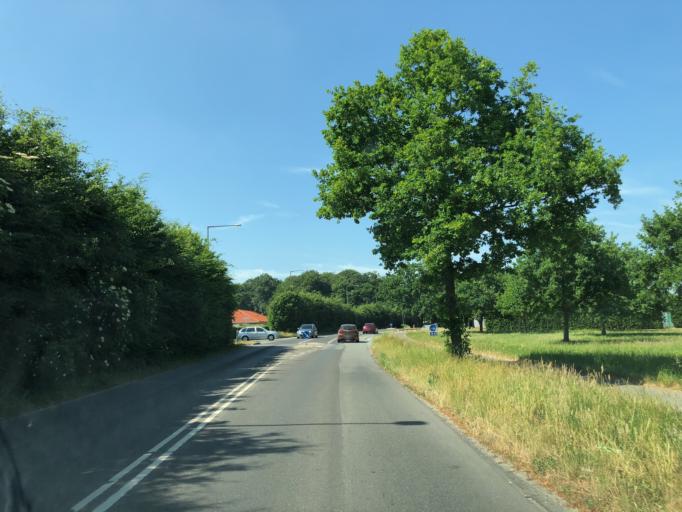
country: DK
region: South Denmark
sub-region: Kolding Kommune
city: Kolding
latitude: 55.5079
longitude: 9.5014
